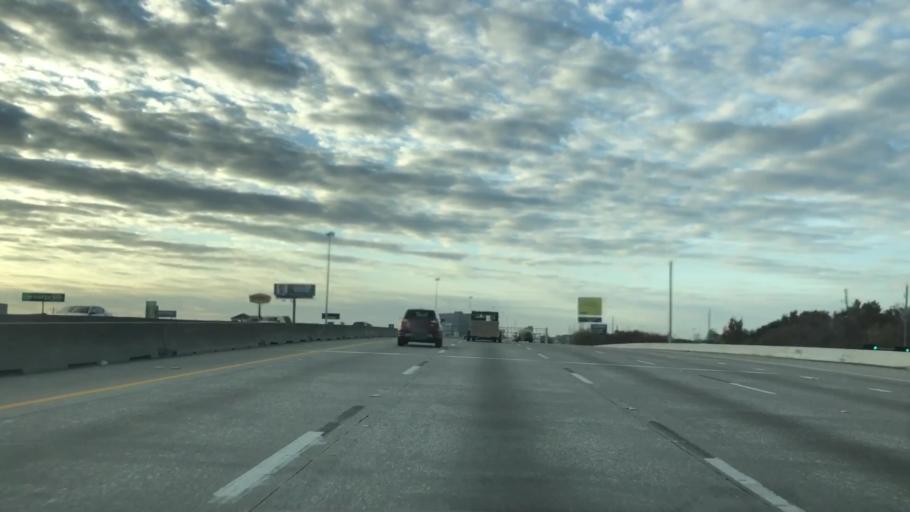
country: US
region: Texas
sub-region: Harris County
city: Aldine
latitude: 29.9325
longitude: -95.4120
